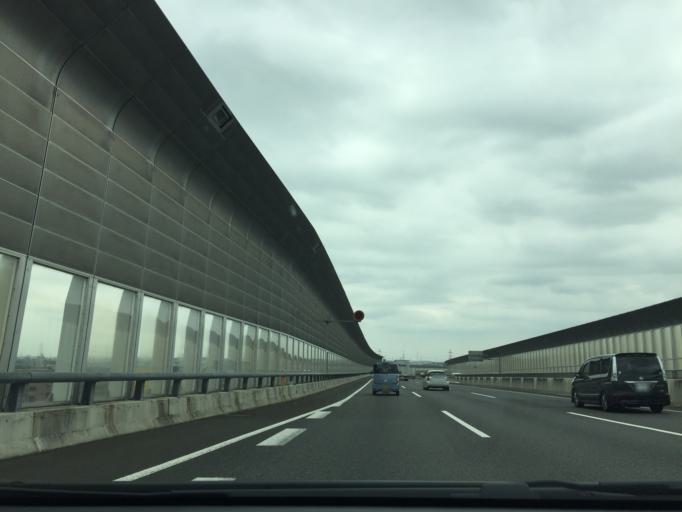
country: JP
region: Aichi
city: Chiryu
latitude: 35.0420
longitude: 137.0379
